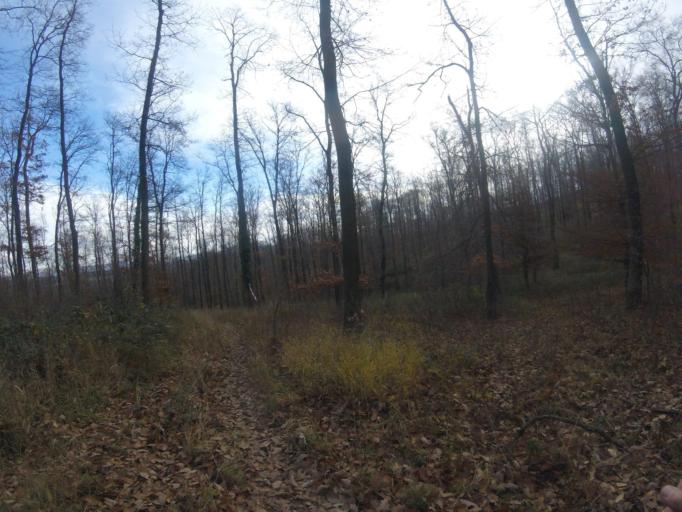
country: HU
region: Veszprem
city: Sumeg
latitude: 46.8865
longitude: 17.3337
